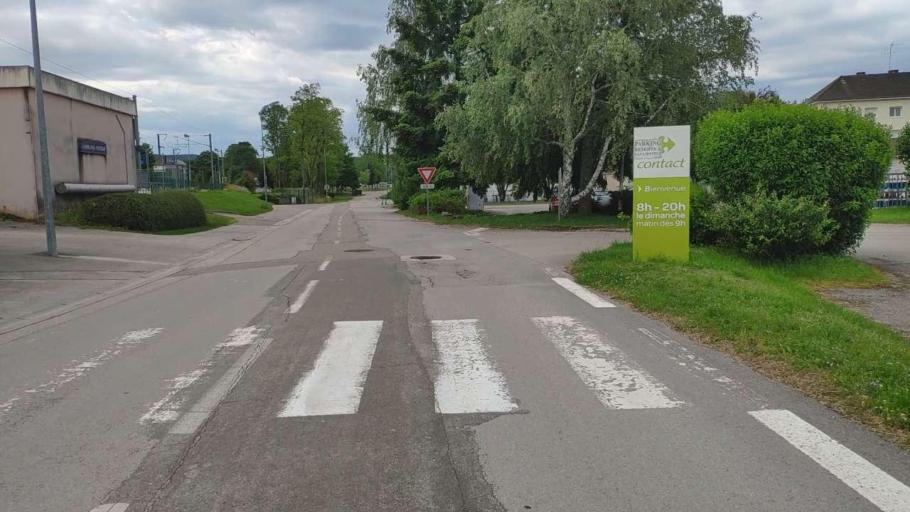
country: FR
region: Franche-Comte
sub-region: Departement du Jura
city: Perrigny
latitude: 46.7630
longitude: 5.5975
